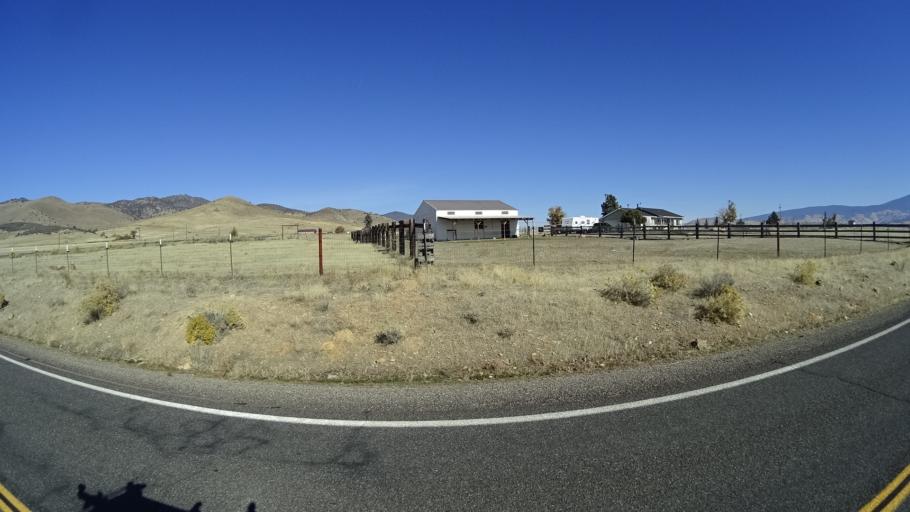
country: US
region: California
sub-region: Siskiyou County
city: Montague
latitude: 41.7712
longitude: -122.5236
